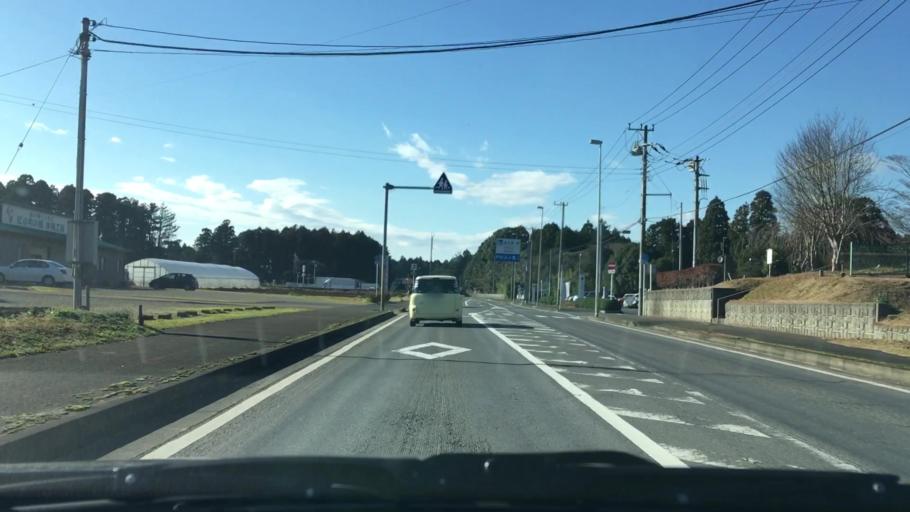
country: JP
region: Chiba
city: Sawara
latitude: 35.8062
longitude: 140.4712
